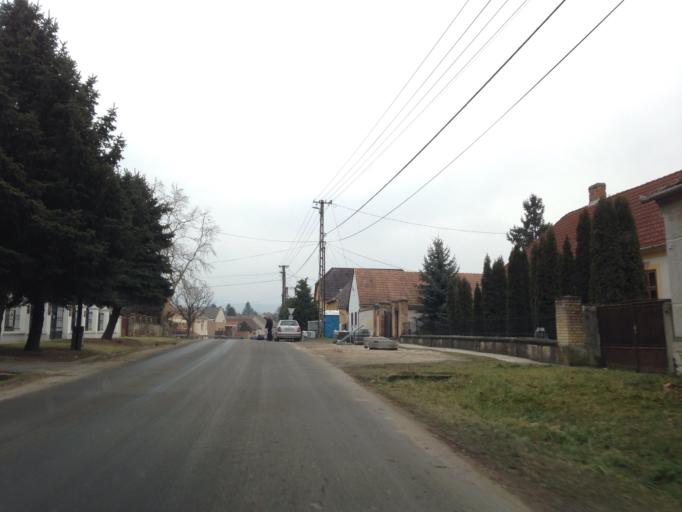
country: HU
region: Komarom-Esztergom
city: Szomod
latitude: 47.6841
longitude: 18.3402
